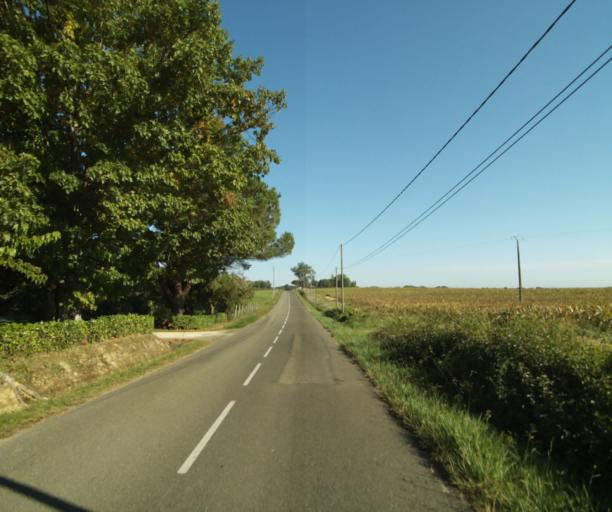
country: FR
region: Aquitaine
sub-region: Departement des Landes
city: Gabarret
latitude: 43.9226
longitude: 0.0175
